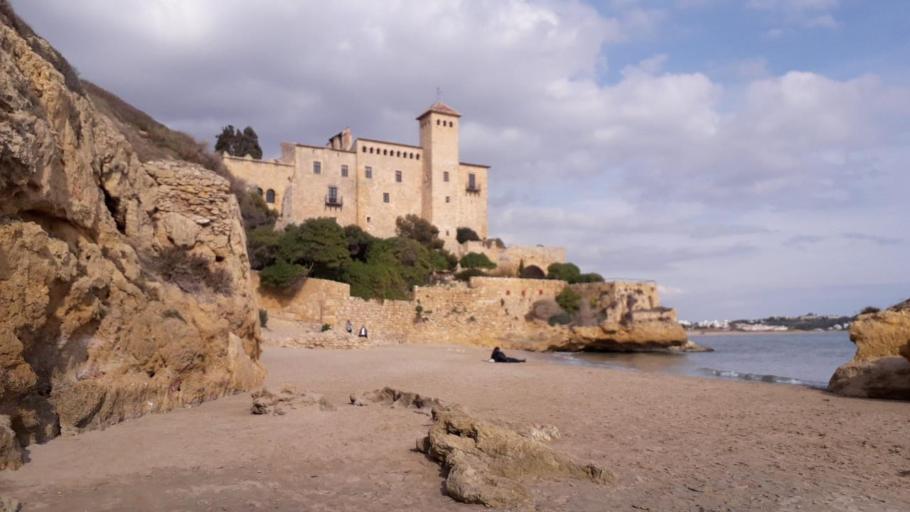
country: ES
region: Catalonia
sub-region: Provincia de Tarragona
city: Altafulla
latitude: 41.1293
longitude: 1.3604
